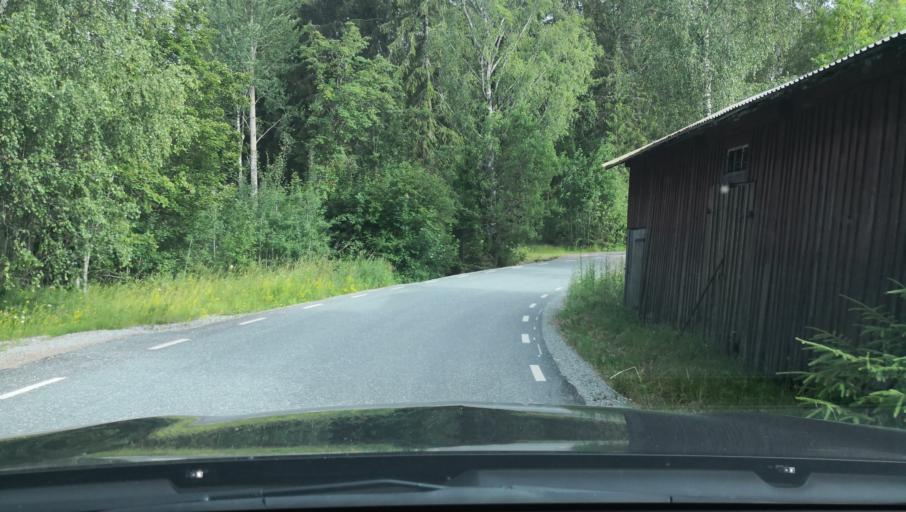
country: SE
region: Vaestmanland
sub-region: Surahammars Kommun
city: Surahammar
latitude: 59.6604
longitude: 16.1772
